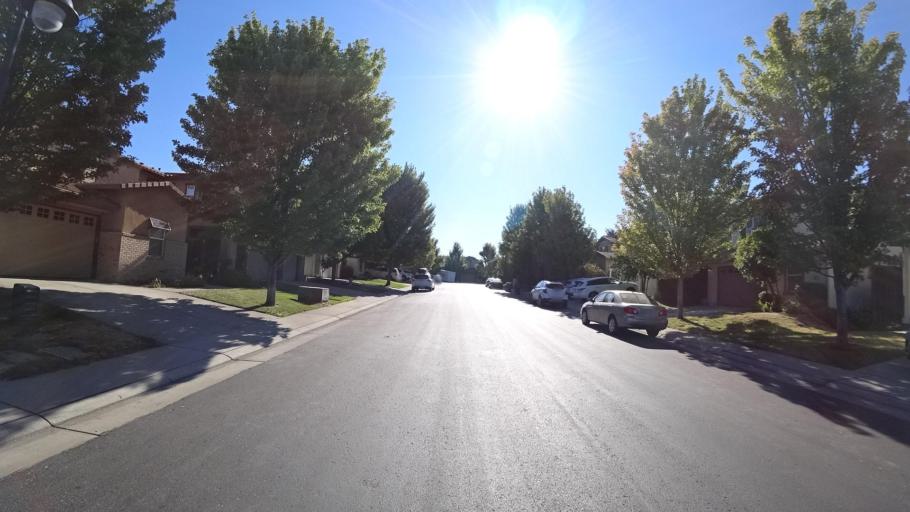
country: US
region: California
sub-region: Placer County
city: Rocklin
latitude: 38.8303
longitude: -121.2729
